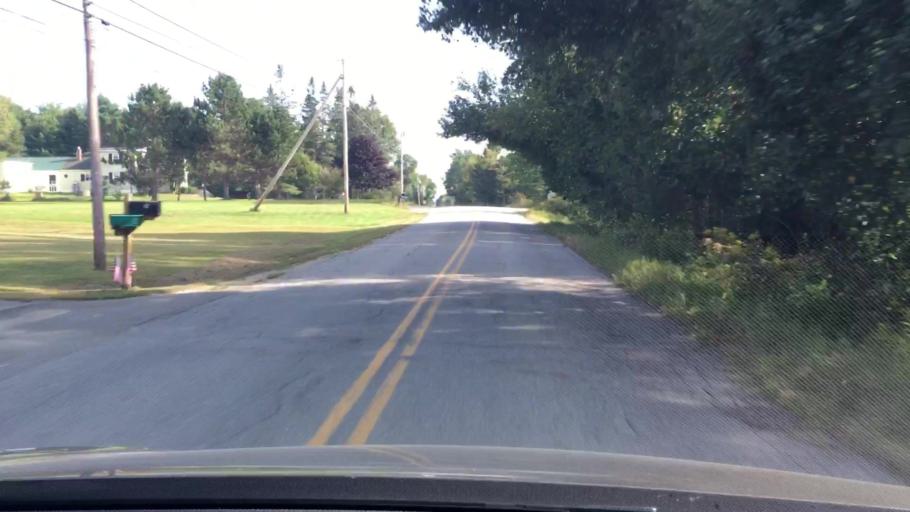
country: US
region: Maine
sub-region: Hancock County
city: Bucksport
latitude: 44.5469
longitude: -68.7972
